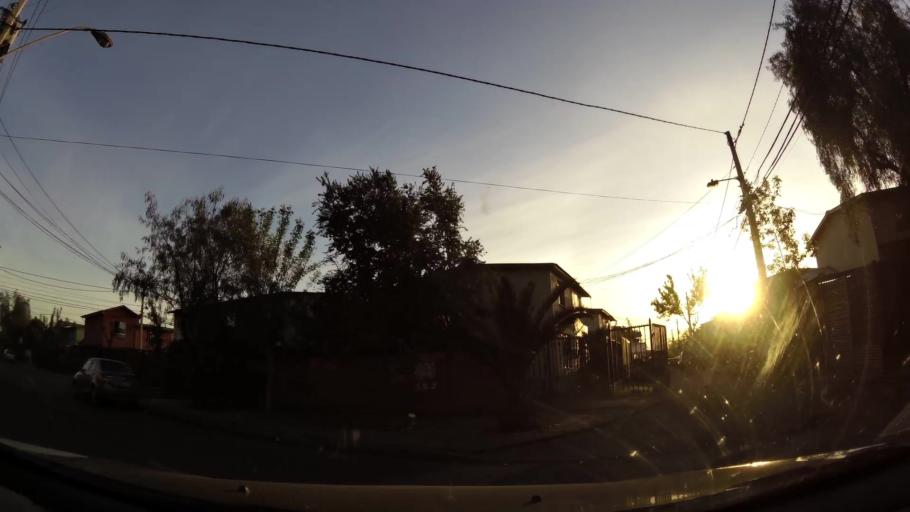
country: CL
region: Santiago Metropolitan
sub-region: Provincia de Cordillera
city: Puente Alto
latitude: -33.5978
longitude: -70.5687
